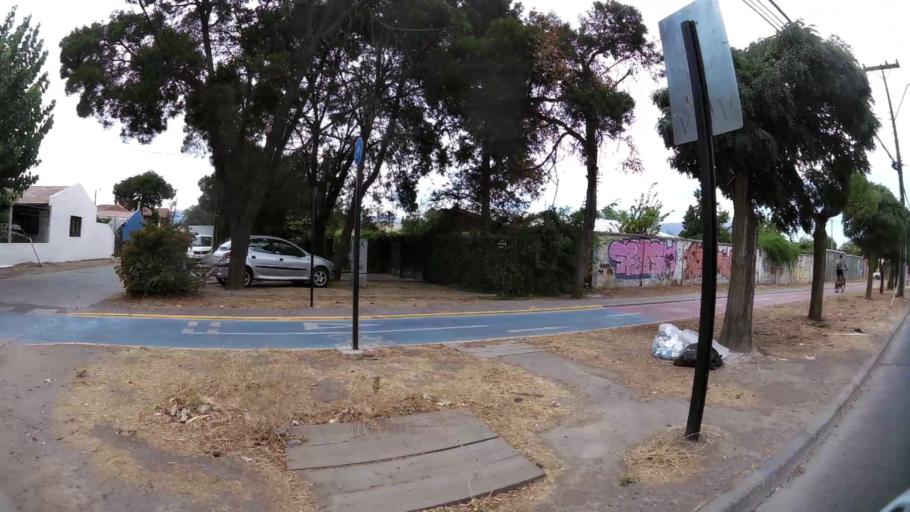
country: CL
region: O'Higgins
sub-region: Provincia de Cachapoal
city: Rancagua
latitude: -34.1514
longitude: -70.7371
